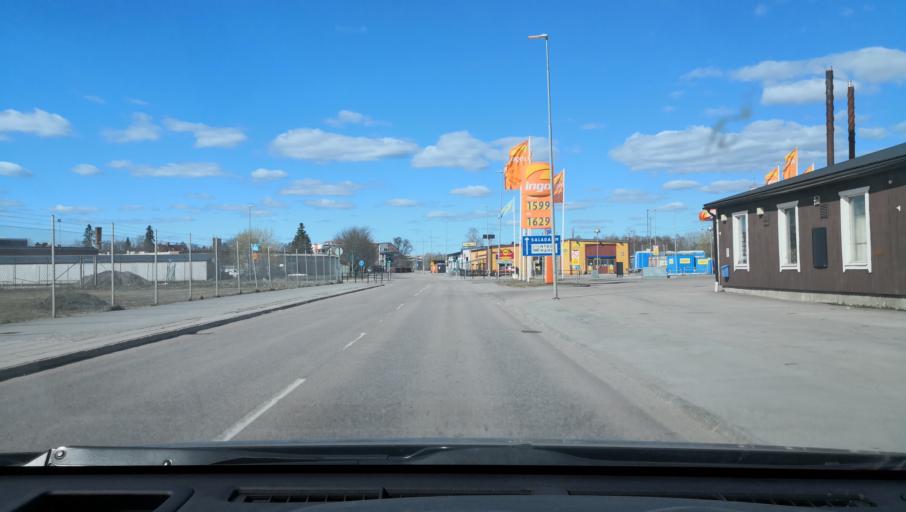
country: SE
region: Vaestmanland
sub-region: Sala Kommun
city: Sala
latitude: 59.9179
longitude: 16.6163
